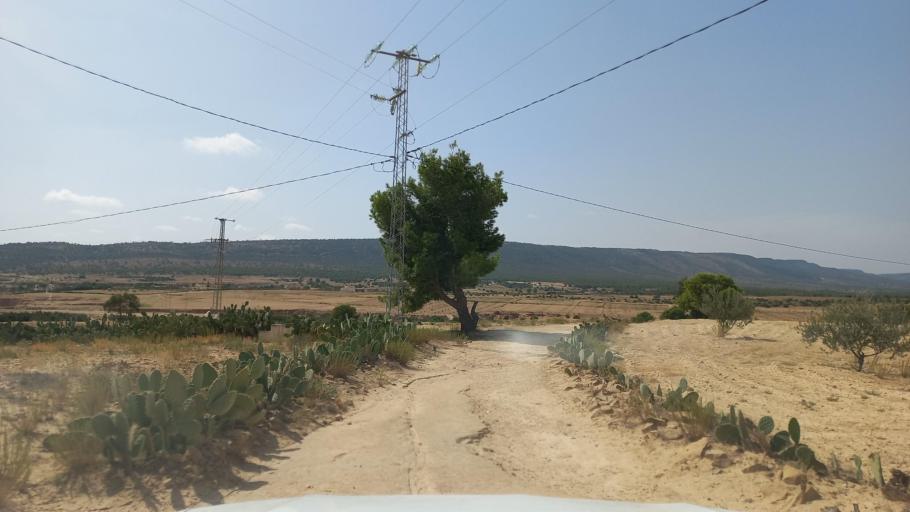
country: TN
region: Al Qasrayn
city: Sbiba
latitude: 35.3951
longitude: 8.9575
